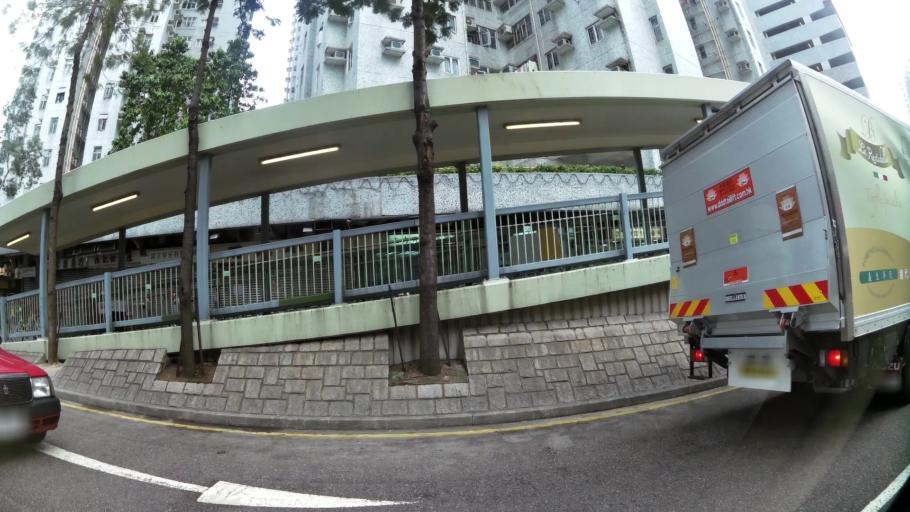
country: HK
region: Wanchai
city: Wan Chai
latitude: 22.2625
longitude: 114.2507
